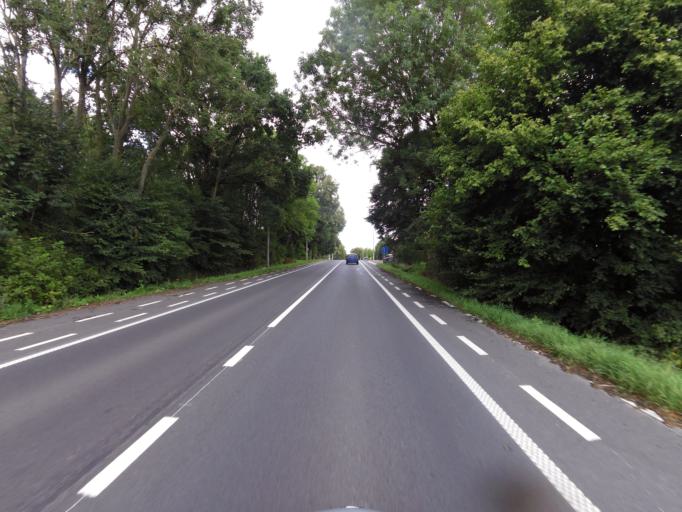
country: BE
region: Wallonia
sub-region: Province du Hainaut
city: Mons
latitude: 50.4419
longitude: 3.9874
